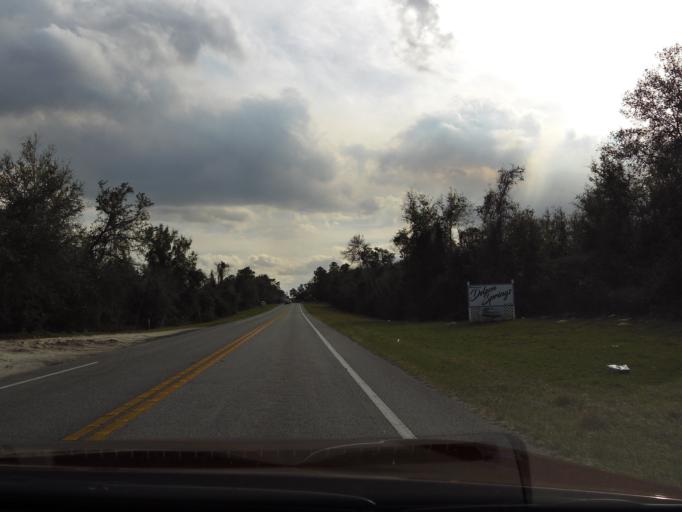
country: US
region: Florida
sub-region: Volusia County
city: De Leon Springs
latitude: 29.1298
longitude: -81.3516
